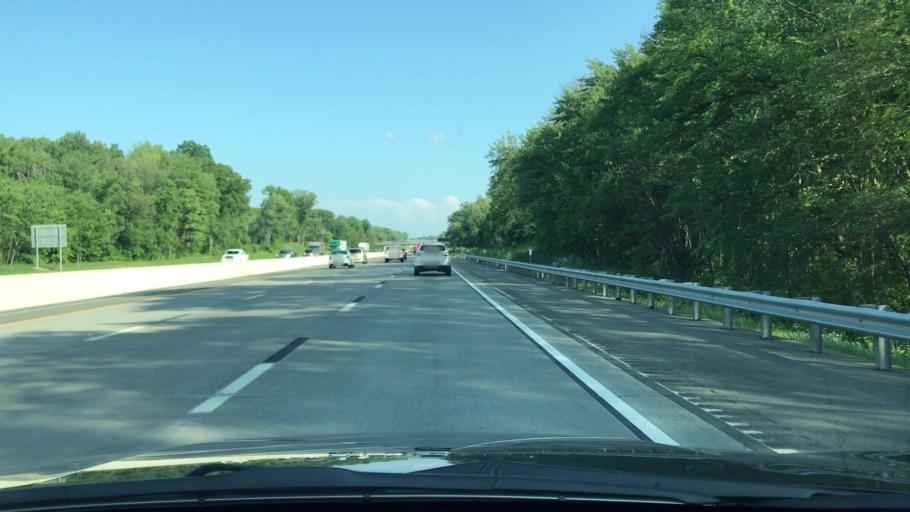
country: US
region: New York
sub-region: Albany County
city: McKownville
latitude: 42.6699
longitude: -73.8380
